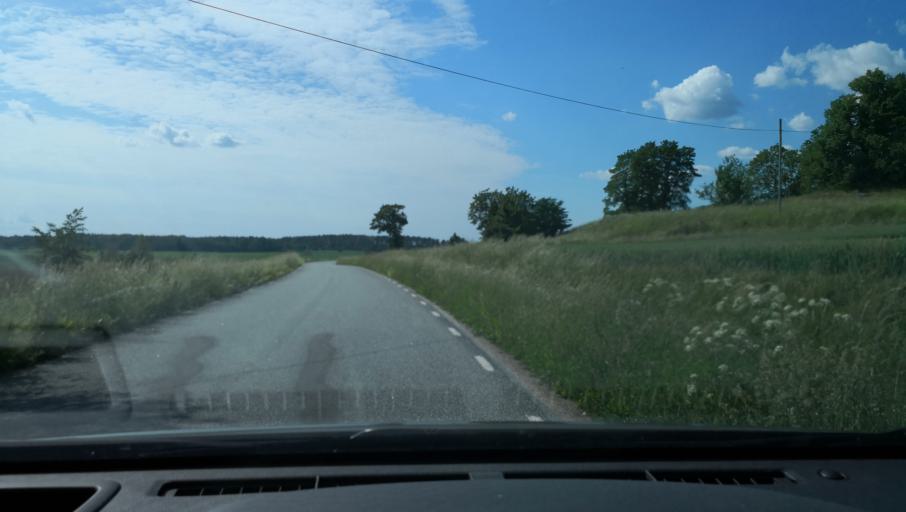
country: SE
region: Uppsala
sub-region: Enkopings Kommun
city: Orsundsbro
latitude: 59.8355
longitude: 17.3067
